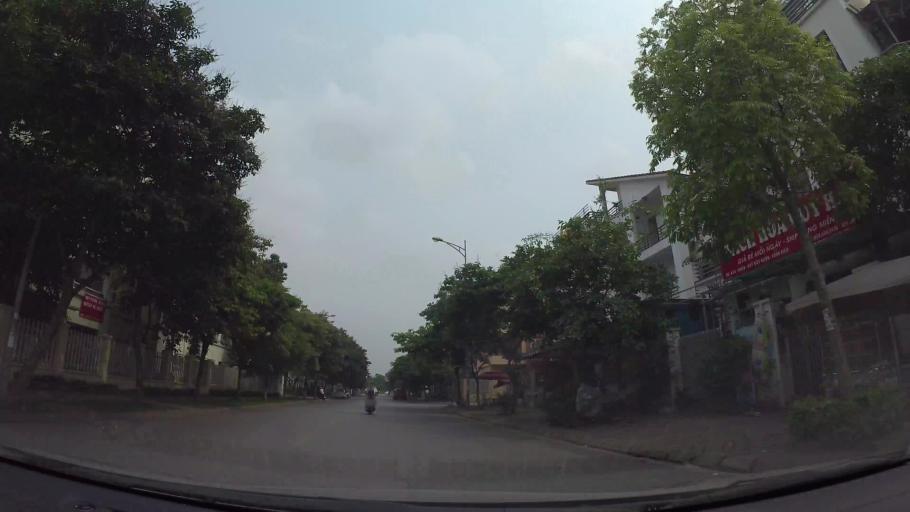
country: VN
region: Ha Noi
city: Trau Quy
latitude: 21.0556
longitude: 105.9089
